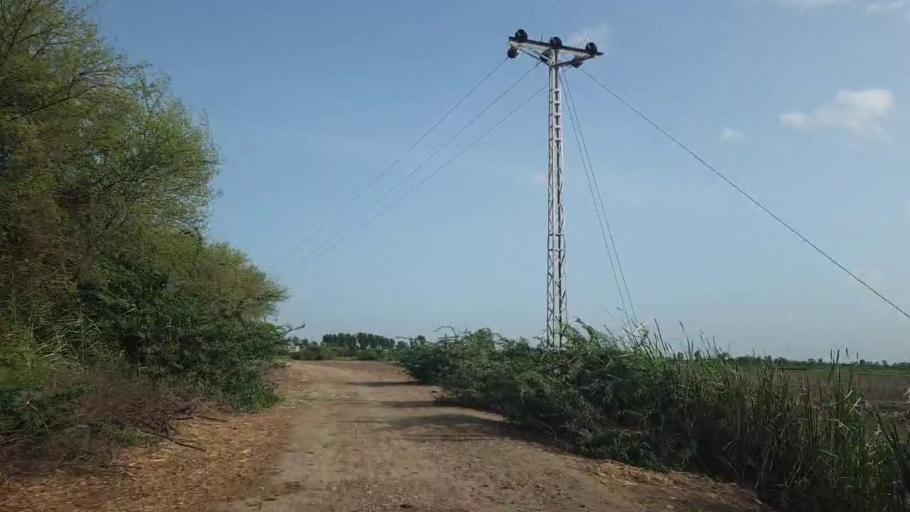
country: PK
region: Sindh
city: Kadhan
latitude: 24.6258
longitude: 69.0844
